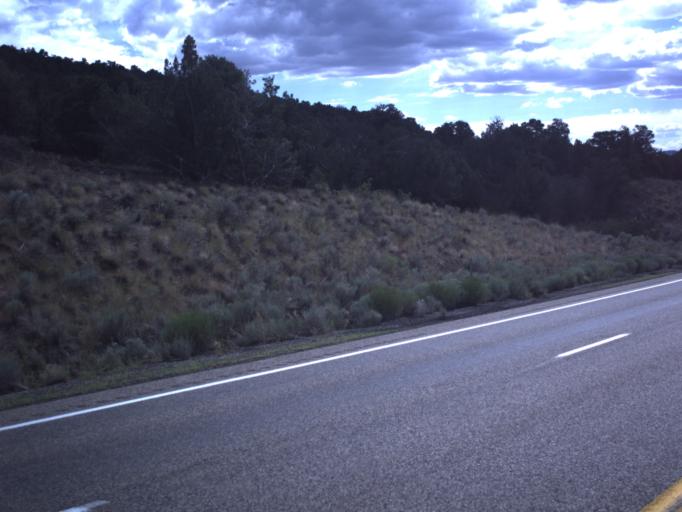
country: US
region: Utah
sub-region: Beaver County
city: Beaver
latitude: 38.0601
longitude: -112.6373
